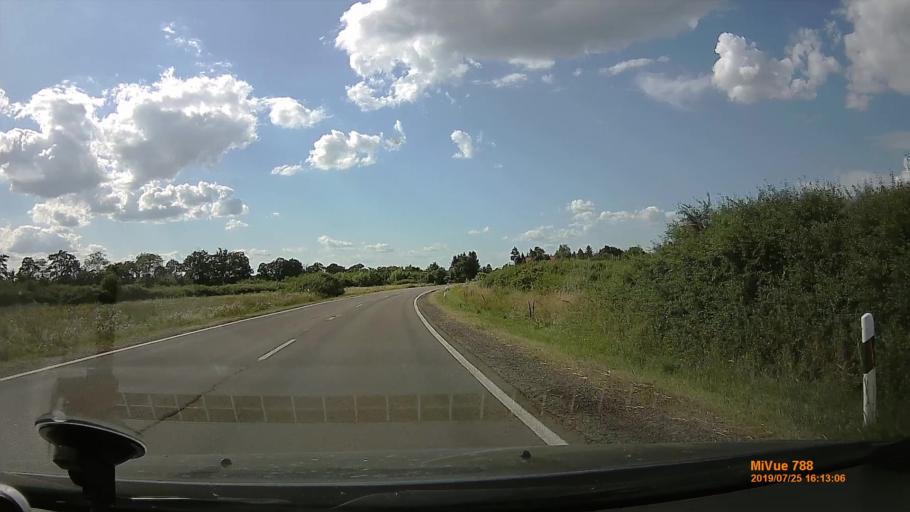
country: HU
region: Heves
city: Kerecsend
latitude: 47.7894
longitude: 20.3437
